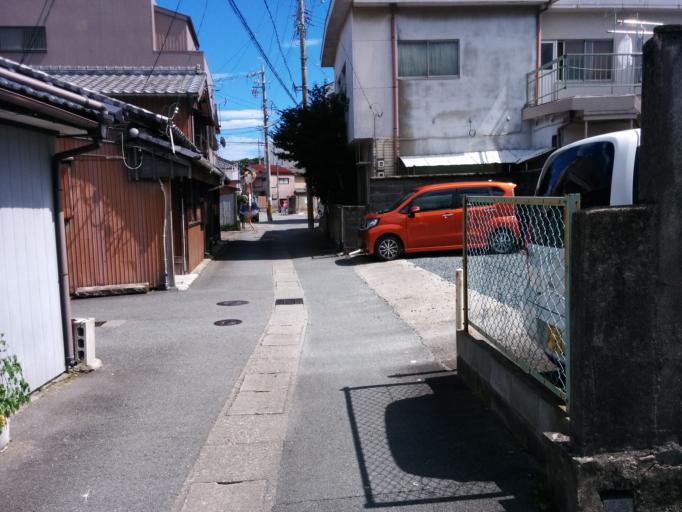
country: JP
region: Mie
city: Ise
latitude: 34.4902
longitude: 136.7061
